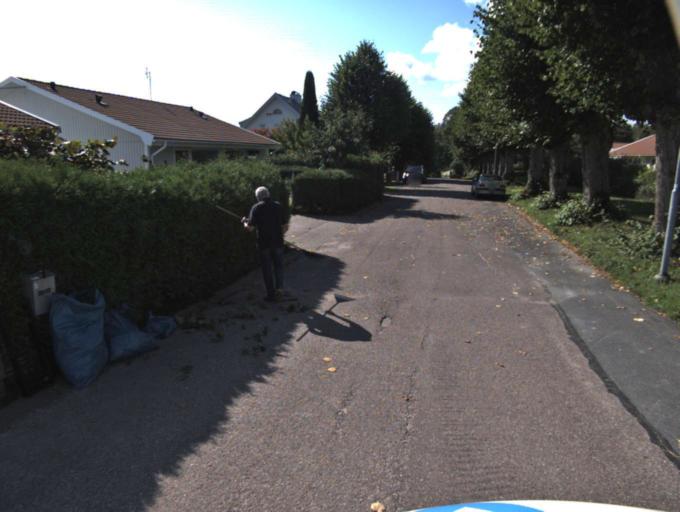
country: SE
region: Vaestra Goetaland
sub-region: Ulricehamns Kommun
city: Ulricehamn
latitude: 57.7985
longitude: 13.3952
